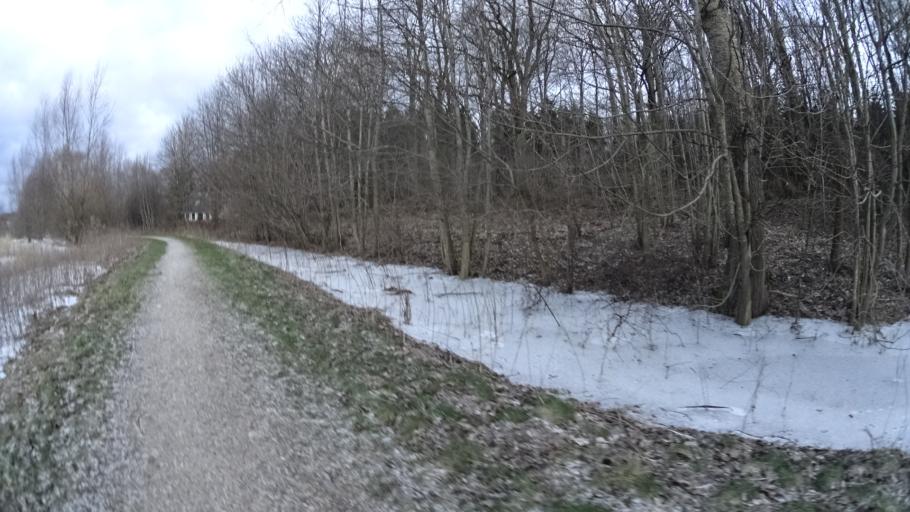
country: DK
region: Central Jutland
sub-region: Arhus Kommune
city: Kolt
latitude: 56.1395
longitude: 10.0704
